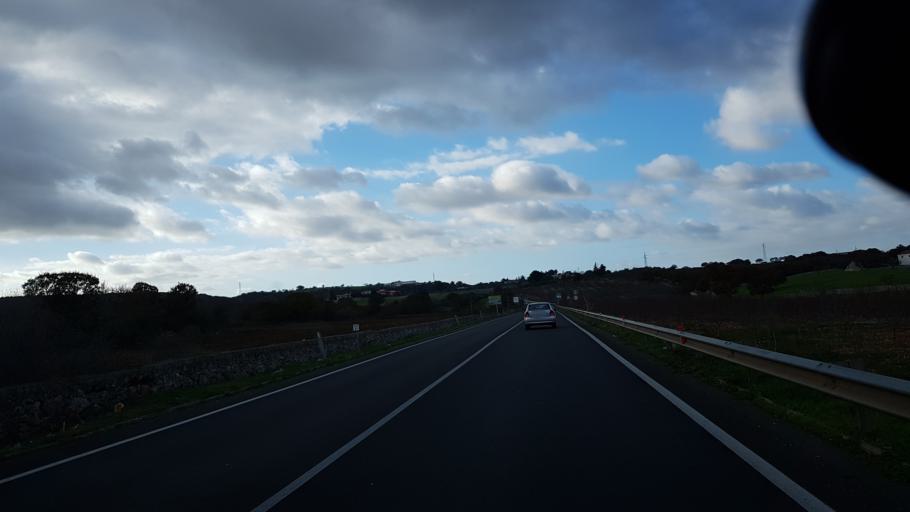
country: IT
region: Apulia
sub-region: Provincia di Bari
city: Alberobello
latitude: 40.8244
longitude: 17.1920
